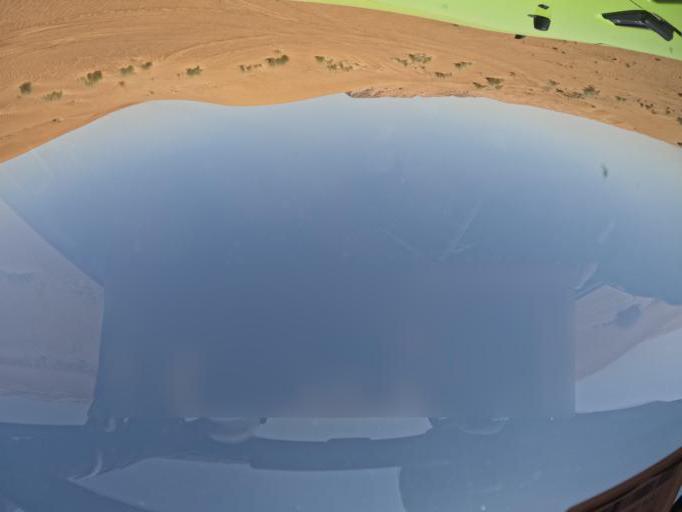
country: AE
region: Ash Shariqah
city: Adh Dhayd
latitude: 25.0191
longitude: 55.7442
